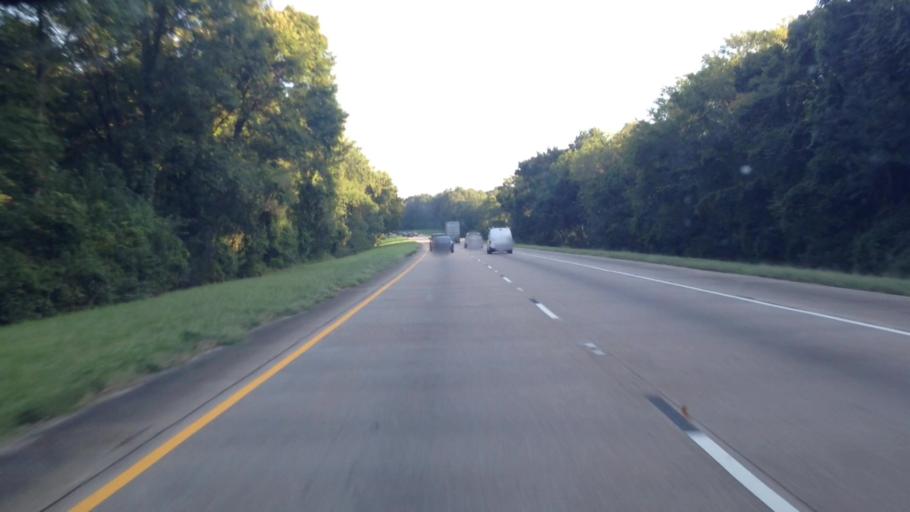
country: US
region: Louisiana
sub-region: Ascension Parish
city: Prairieville
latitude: 30.3033
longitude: -90.9928
